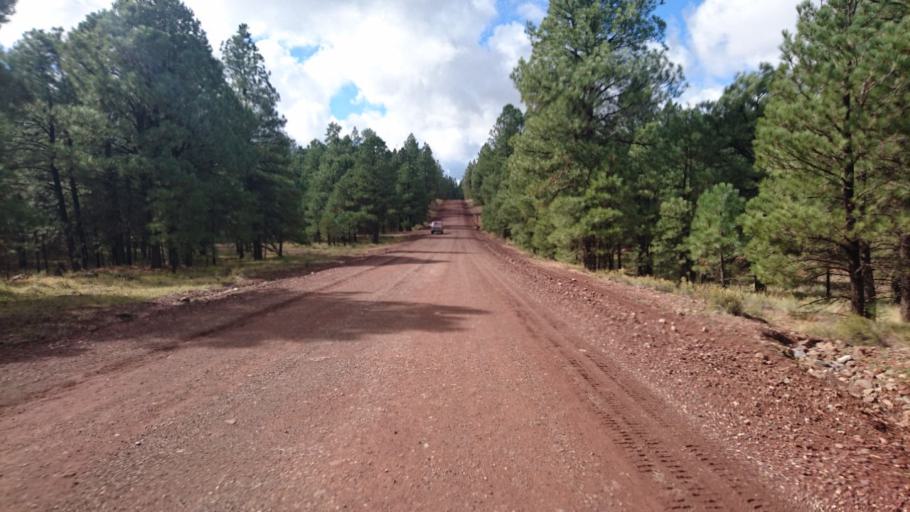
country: US
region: Arizona
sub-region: Coconino County
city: Parks
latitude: 35.2648
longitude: -111.9142
